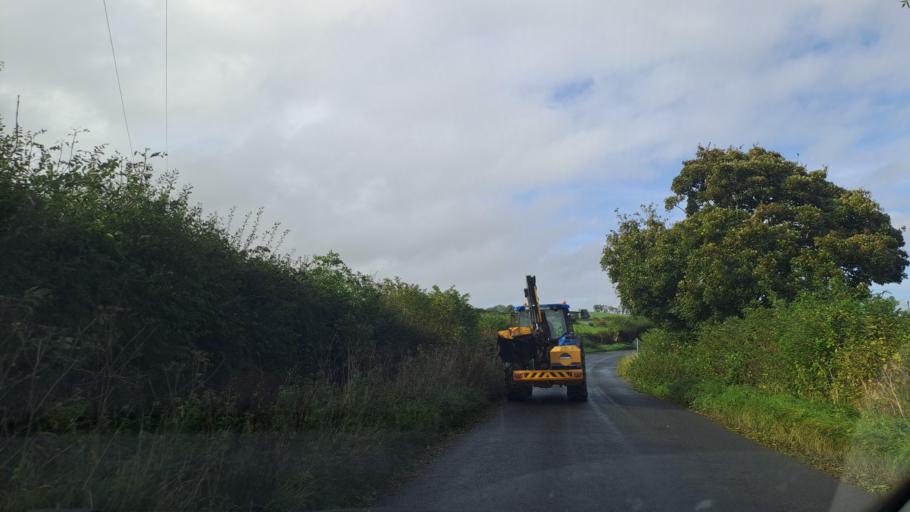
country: IE
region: Ulster
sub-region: County Monaghan
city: Carrickmacross
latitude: 53.8750
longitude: -6.6697
